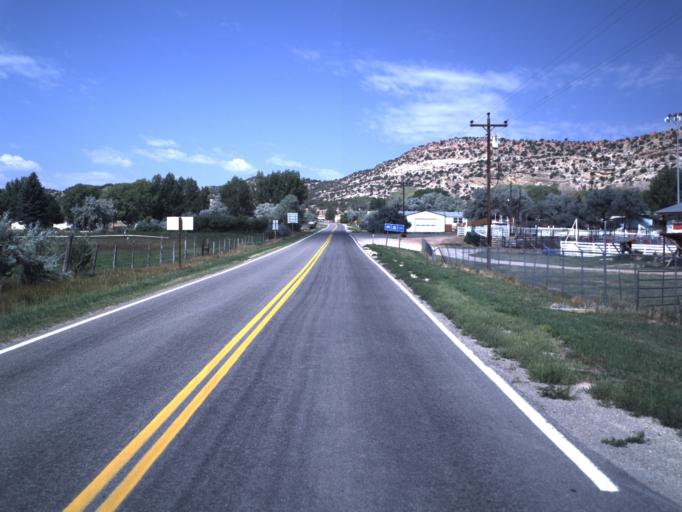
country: US
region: Utah
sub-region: Daggett County
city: Manila
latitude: 40.9883
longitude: -109.7252
